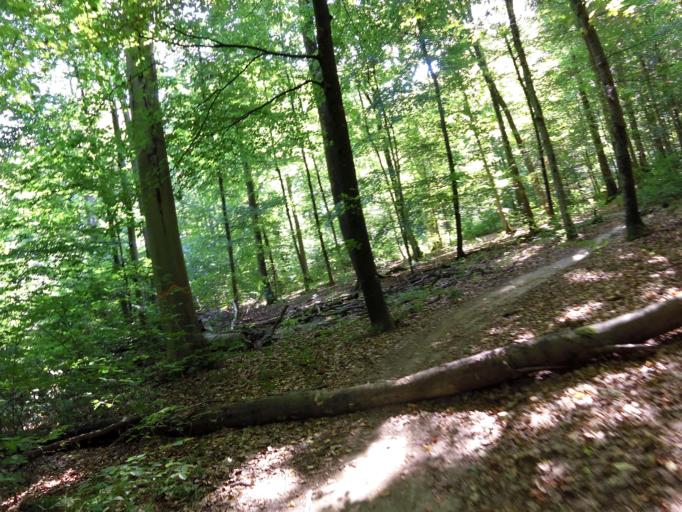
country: DE
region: Bavaria
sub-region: Regierungsbezirk Unterfranken
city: Wuerzburg
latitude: 49.7527
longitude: 9.8841
